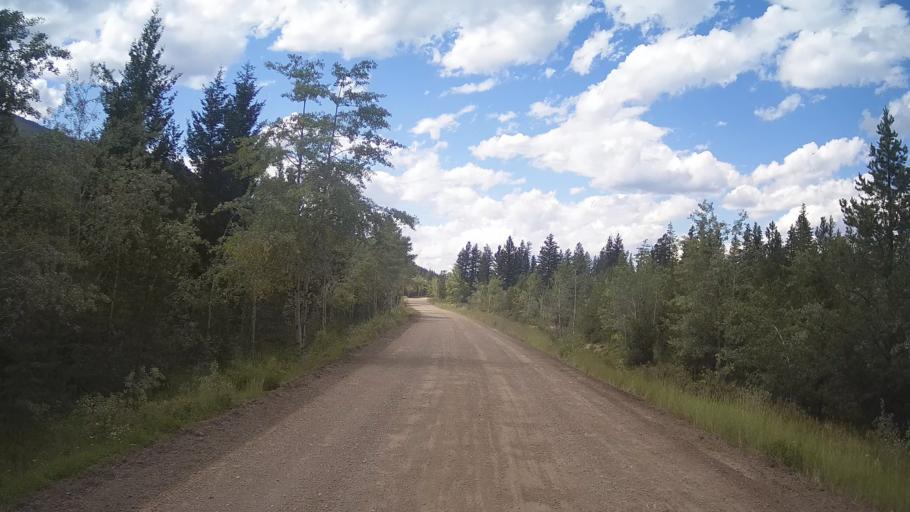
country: CA
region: British Columbia
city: Lillooet
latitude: 51.3249
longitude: -121.8737
